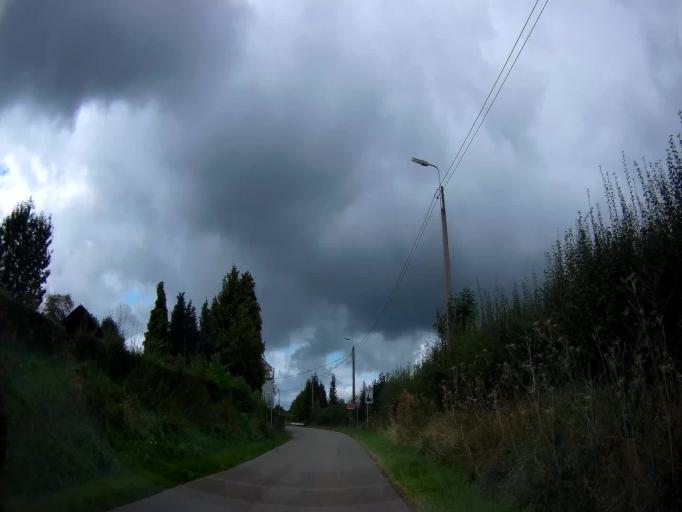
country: BE
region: Wallonia
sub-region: Province de Liege
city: Limbourg
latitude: 50.5951
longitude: 5.9169
